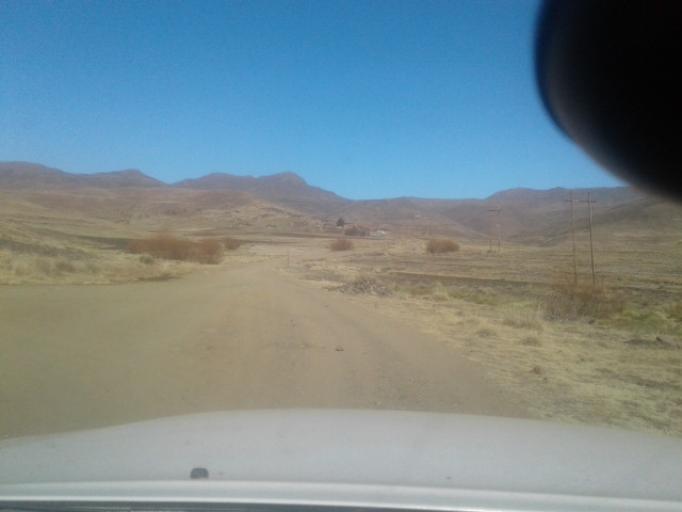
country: LS
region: Maseru
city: Nako
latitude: -29.3766
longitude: 28.0181
